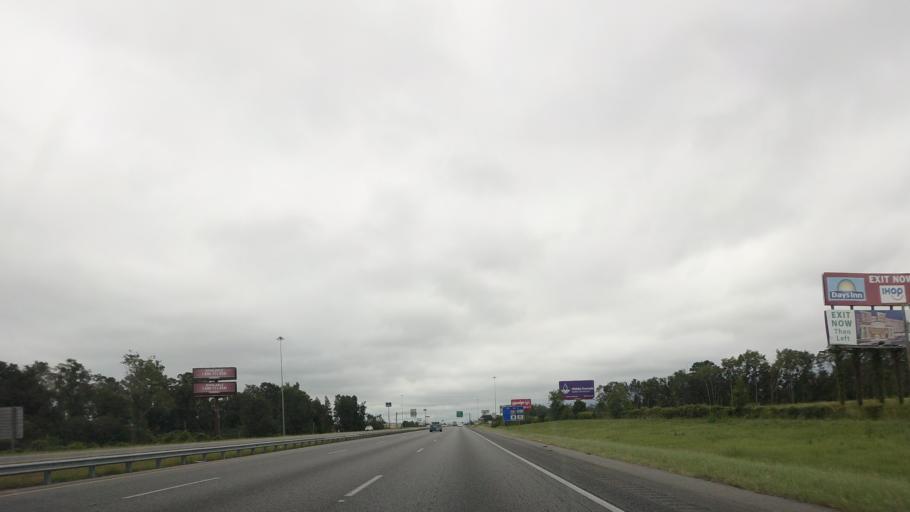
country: US
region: Georgia
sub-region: Lowndes County
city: Remerton
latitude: 30.8312
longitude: -83.3243
